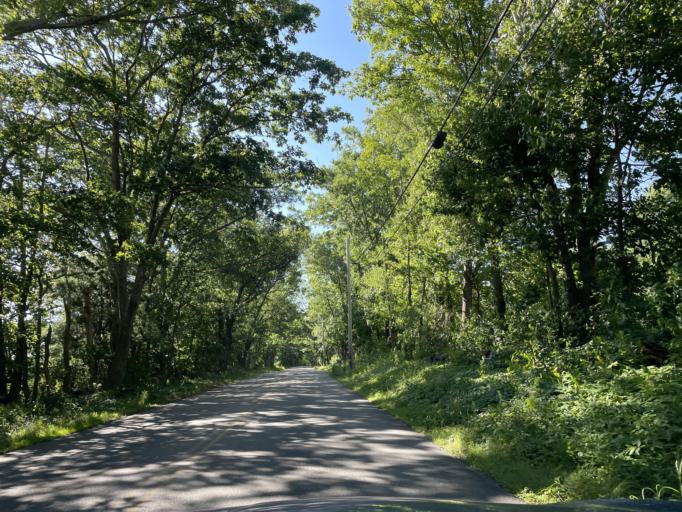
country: US
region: Massachusetts
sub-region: Worcester County
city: Charlton
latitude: 42.1659
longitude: -72.0261
